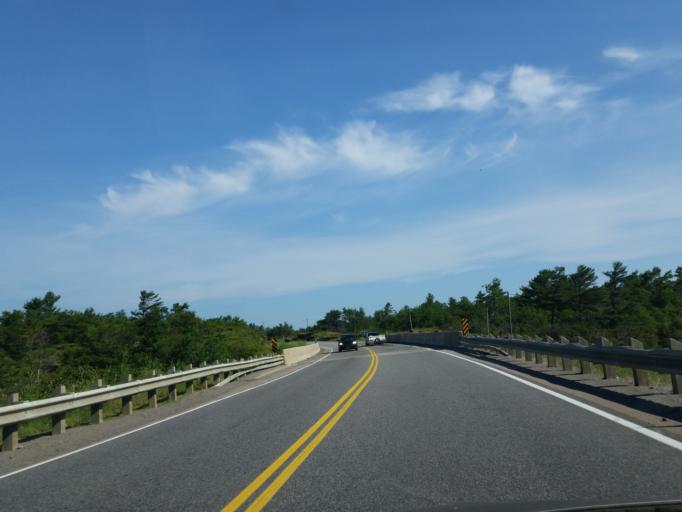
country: CA
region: Ontario
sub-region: Parry Sound District
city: Parry Sound
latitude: 45.7739
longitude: -80.4970
